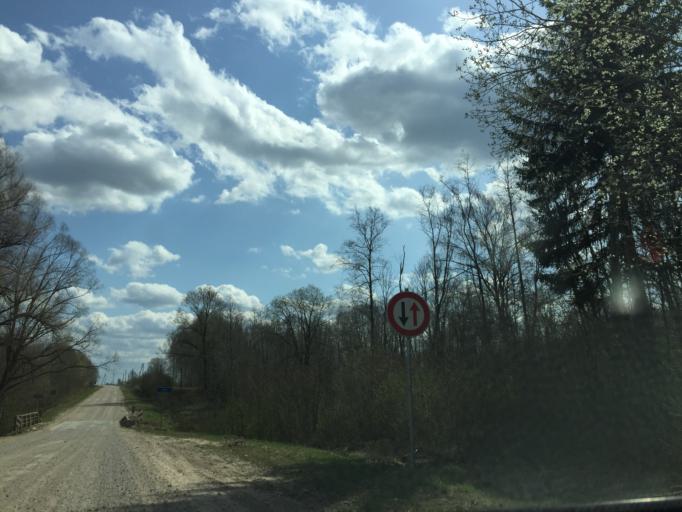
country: LV
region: Skriveri
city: Skriveri
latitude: 56.7484
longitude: 25.0910
